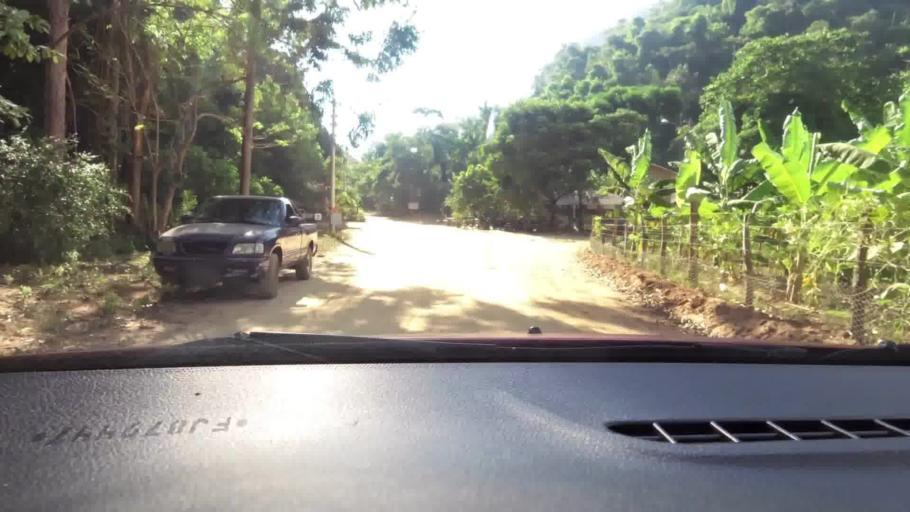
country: BR
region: Espirito Santo
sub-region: Guarapari
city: Guarapari
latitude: -20.5234
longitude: -40.5667
